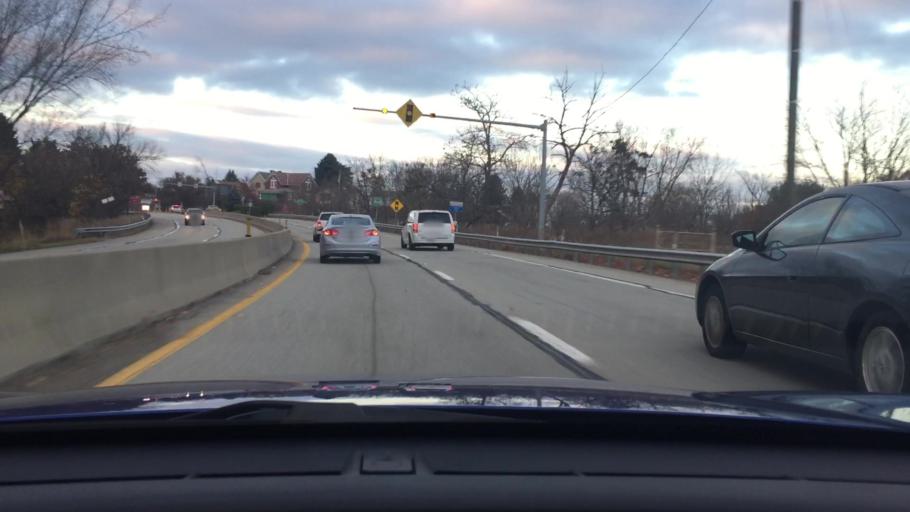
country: US
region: Pennsylvania
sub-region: Westmoreland County
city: South Greensburg
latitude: 40.2713
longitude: -79.5559
